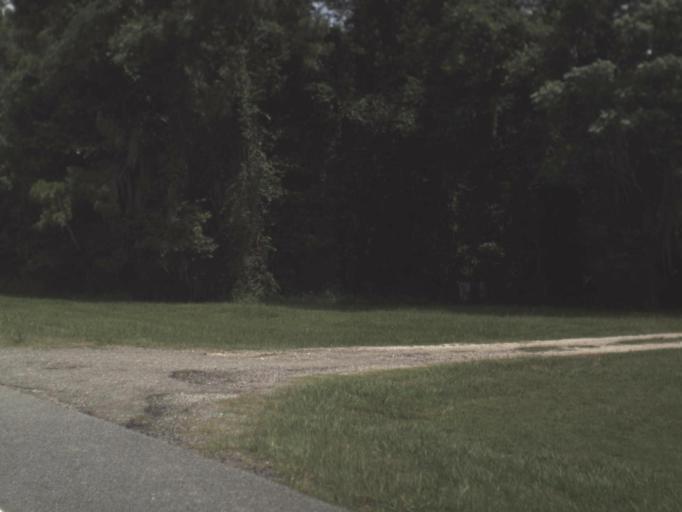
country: US
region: Florida
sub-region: Madison County
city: Madison
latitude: 30.4816
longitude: -83.4496
